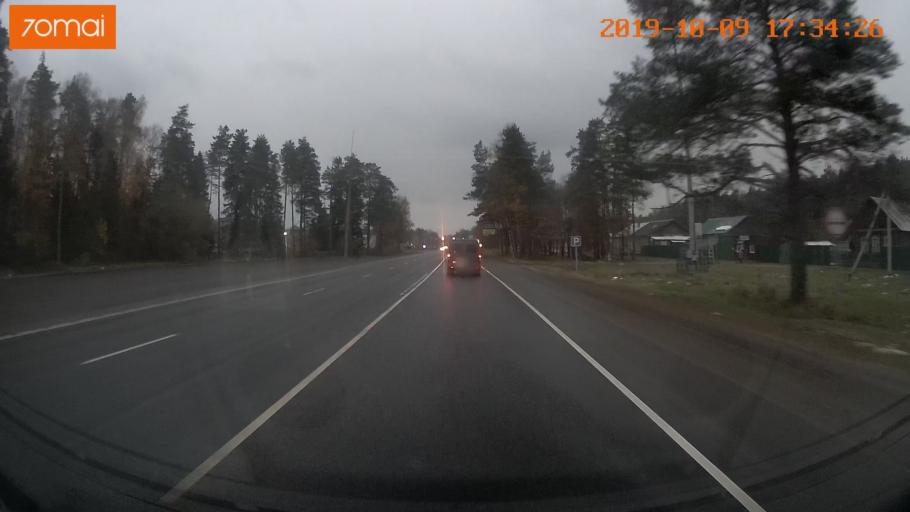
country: RU
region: Ivanovo
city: Bogorodskoye
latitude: 57.1066
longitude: 41.0115
